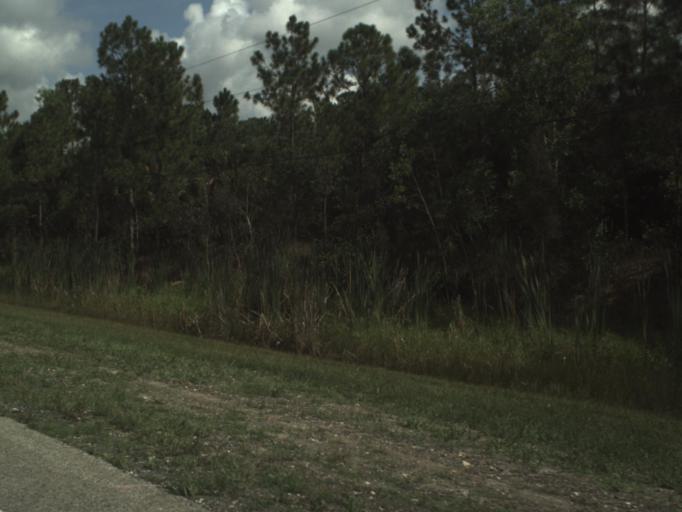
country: US
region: Florida
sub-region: Palm Beach County
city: Palm Beach Gardens
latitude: 26.8806
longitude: -80.2578
